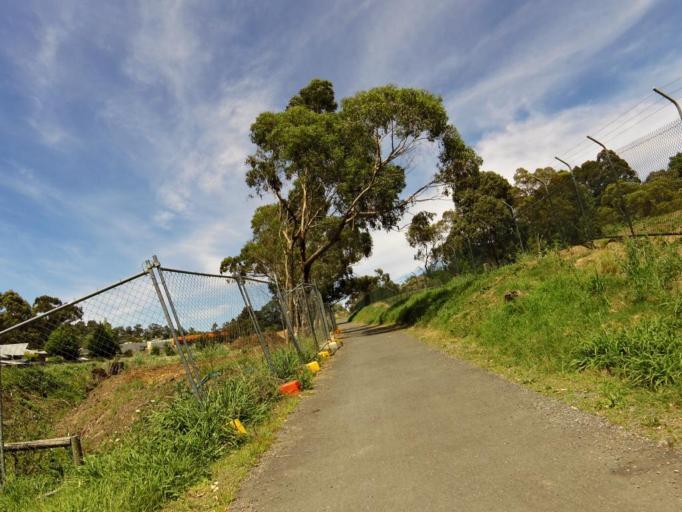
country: AU
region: Victoria
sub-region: Yarra Ranges
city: Lilydale
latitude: -37.7503
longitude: 145.3608
